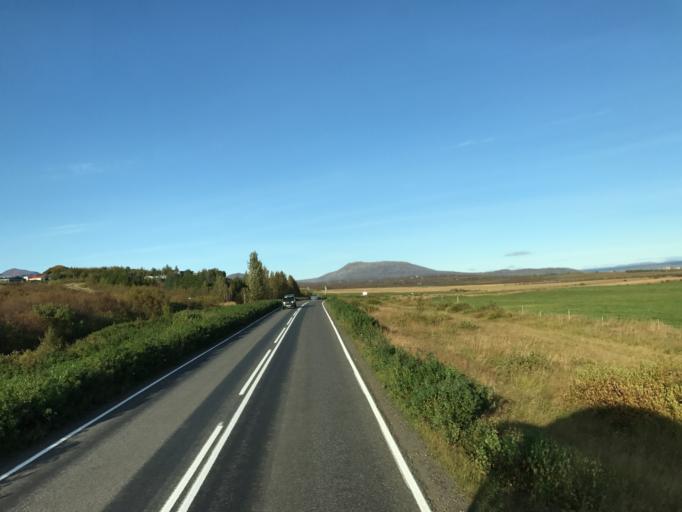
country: IS
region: South
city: Selfoss
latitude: 64.2371
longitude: -20.5543
